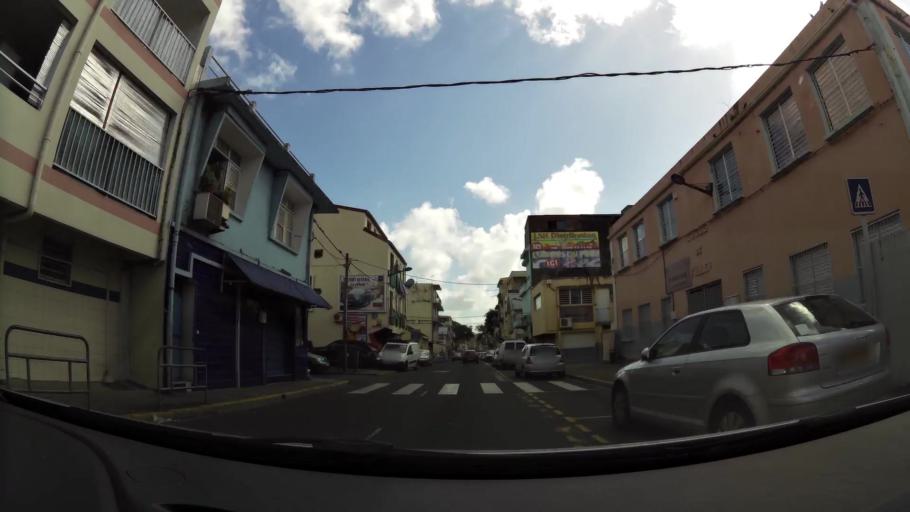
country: MQ
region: Martinique
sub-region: Martinique
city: Fort-de-France
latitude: 14.6133
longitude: -61.0722
